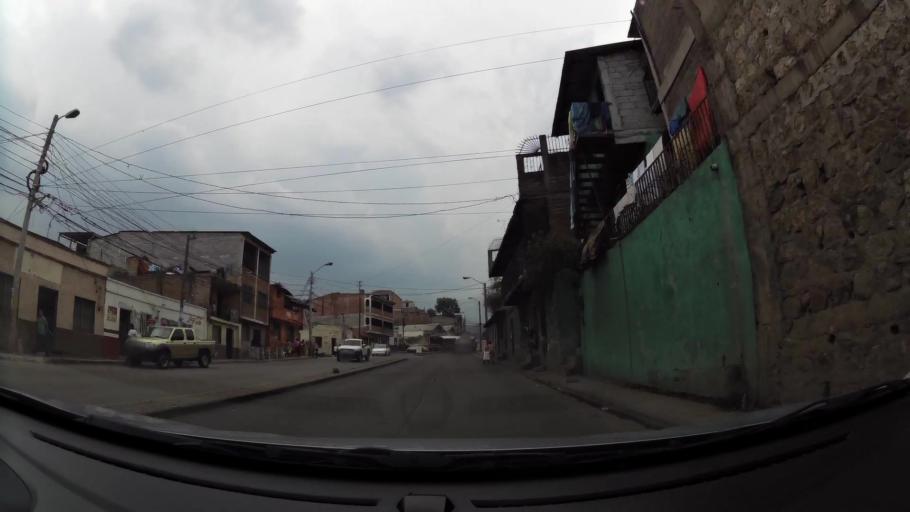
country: HN
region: Francisco Morazan
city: Tegucigalpa
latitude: 14.0937
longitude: -87.2171
